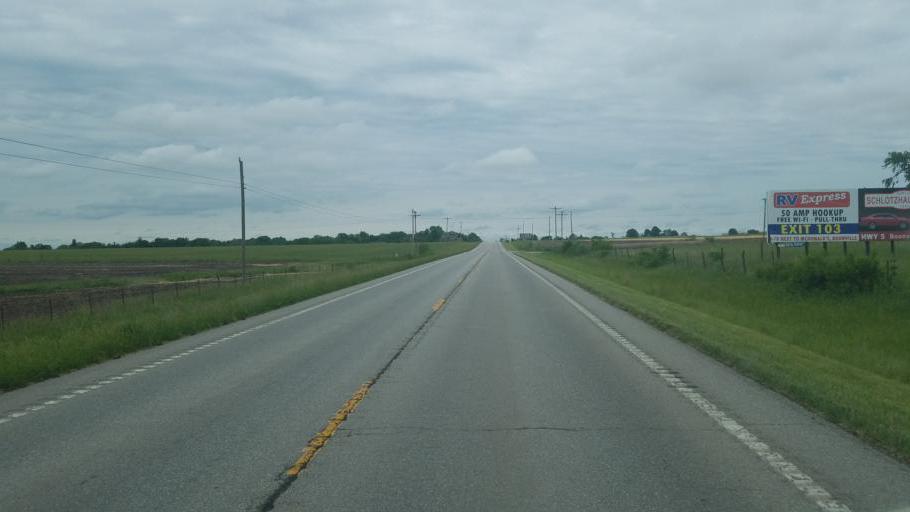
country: US
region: Missouri
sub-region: Morgan County
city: Versailles
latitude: 38.4571
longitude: -92.8092
